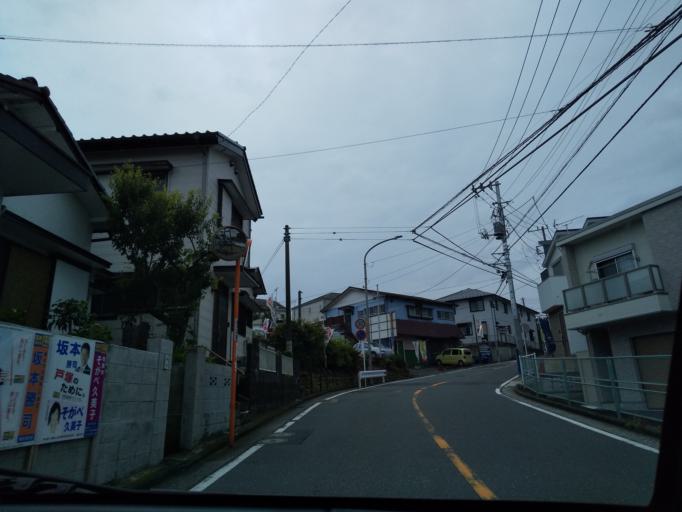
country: JP
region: Kanagawa
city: Fujisawa
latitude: 35.3921
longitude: 139.5074
